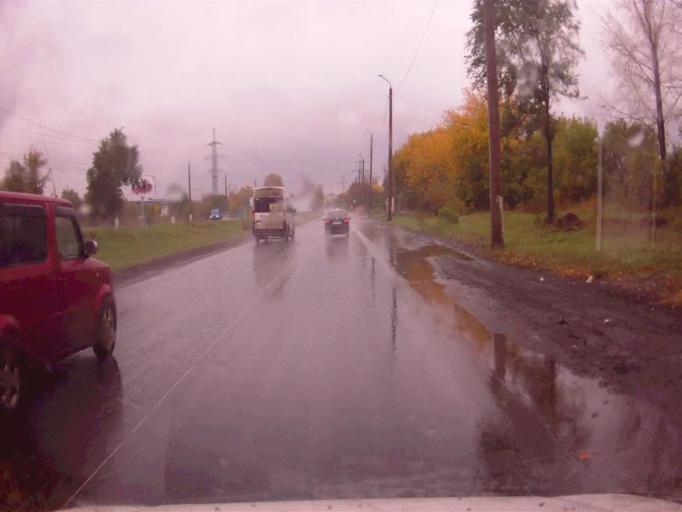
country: RU
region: Chelyabinsk
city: Dolgoderevenskoye
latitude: 55.2455
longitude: 61.3592
